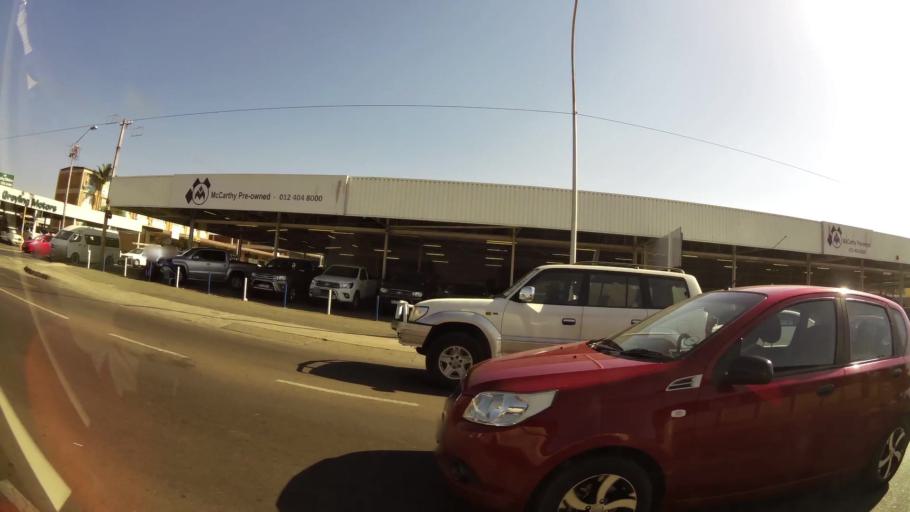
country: ZA
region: Gauteng
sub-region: City of Tshwane Metropolitan Municipality
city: Pretoria
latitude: -25.7179
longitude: 28.2040
